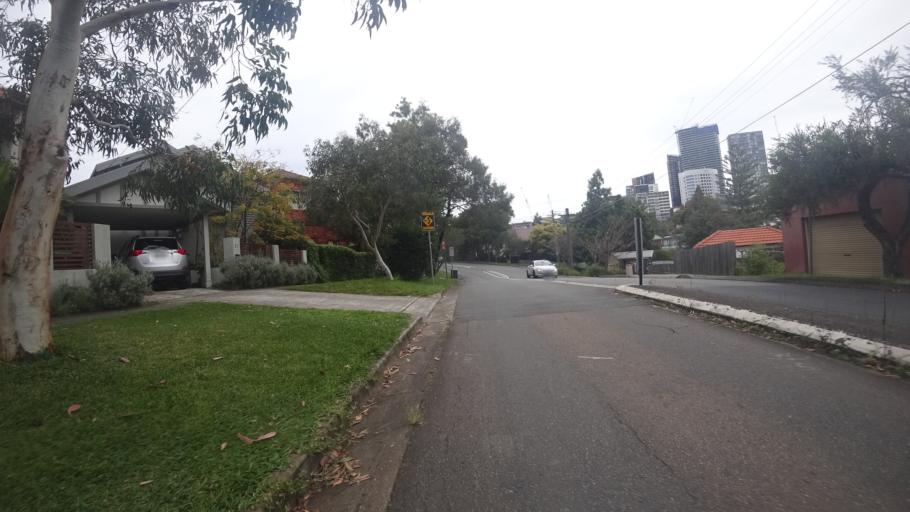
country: AU
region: New South Wales
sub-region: North Sydney
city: St Leonards
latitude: -33.8189
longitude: 151.1980
